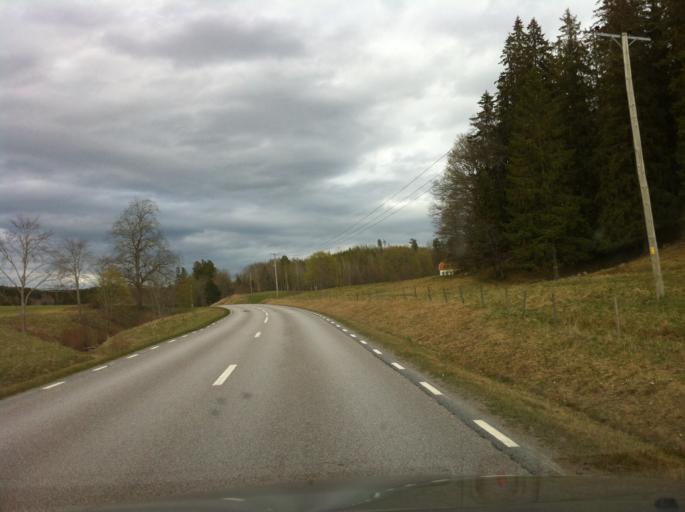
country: SE
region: OEstergoetland
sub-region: Kinda Kommun
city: Rimforsa
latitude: 58.0829
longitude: 15.8279
